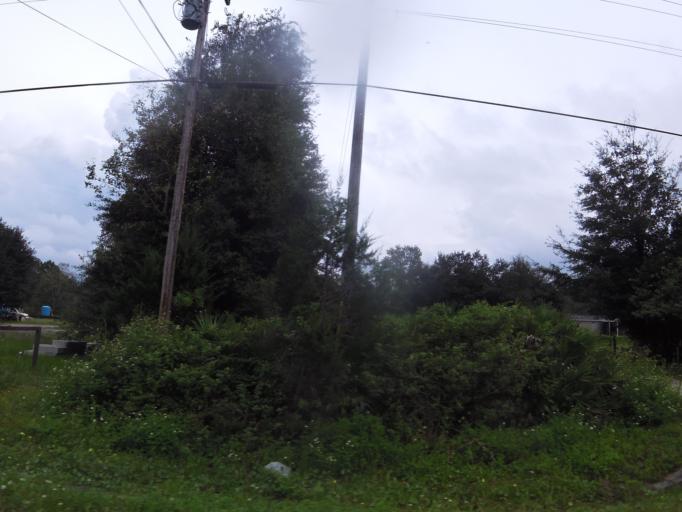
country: US
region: Florida
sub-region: Clay County
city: Middleburg
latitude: 30.1140
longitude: -81.9617
